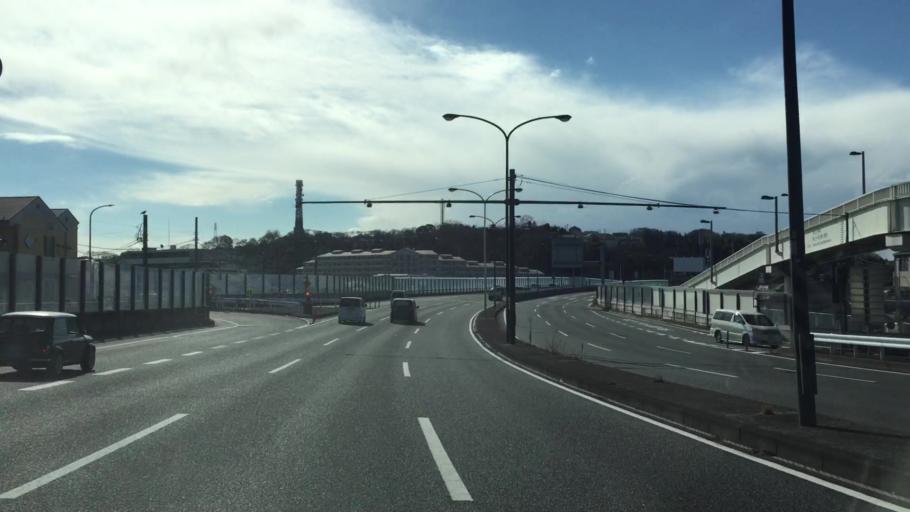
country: JP
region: Kanagawa
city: Yokohama
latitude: 35.4744
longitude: 139.5756
